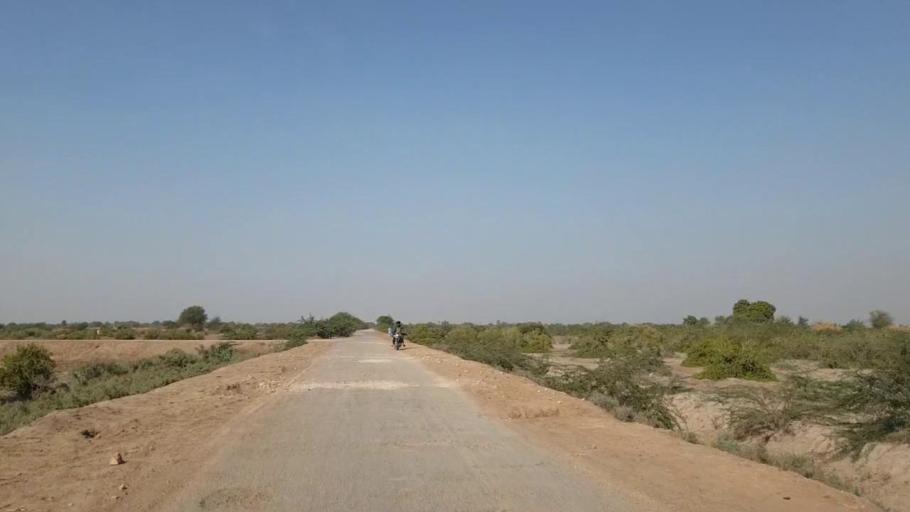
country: PK
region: Sindh
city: Digri
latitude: 24.9832
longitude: 69.1103
